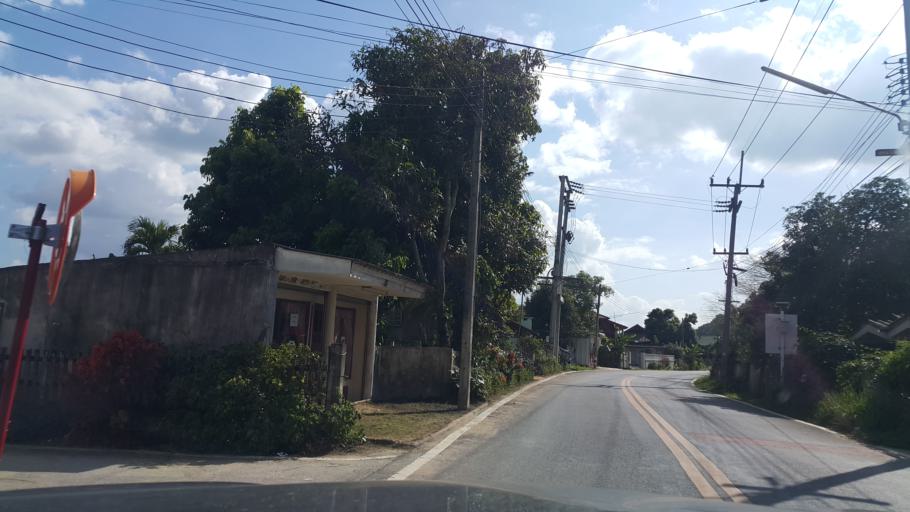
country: TH
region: Lamphun
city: Ban Thi
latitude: 18.5995
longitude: 99.2714
